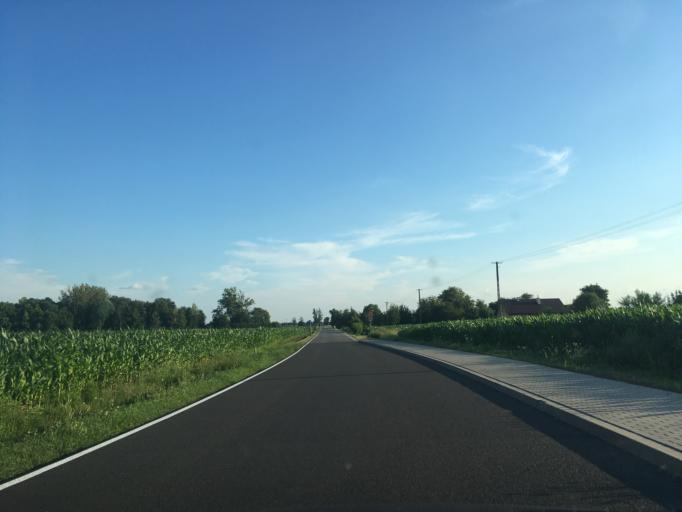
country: PL
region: Masovian Voivodeship
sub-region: Powiat warszawski zachodni
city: Bieniewice
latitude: 52.1401
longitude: 20.5931
